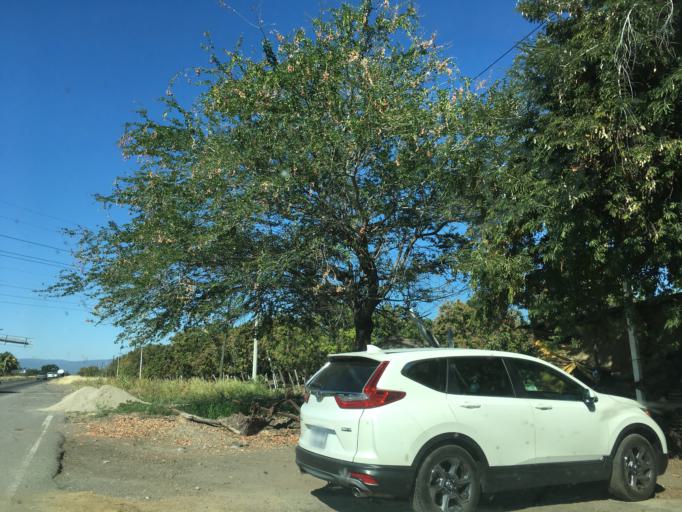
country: MX
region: Michoacan
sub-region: Gabriel Zamora
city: Lombardia
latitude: 19.0974
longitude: -102.0576
